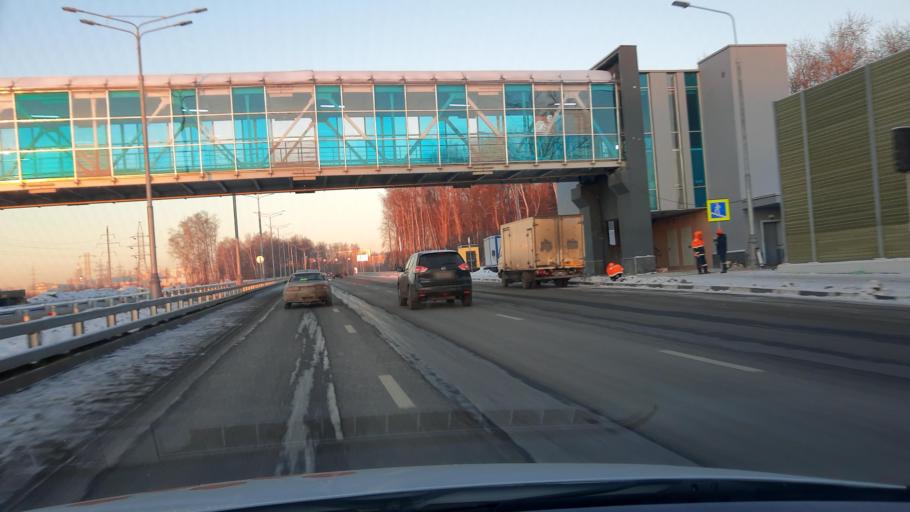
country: RU
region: Moscow
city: Tyoply Stan
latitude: 55.5968
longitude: 37.4840
